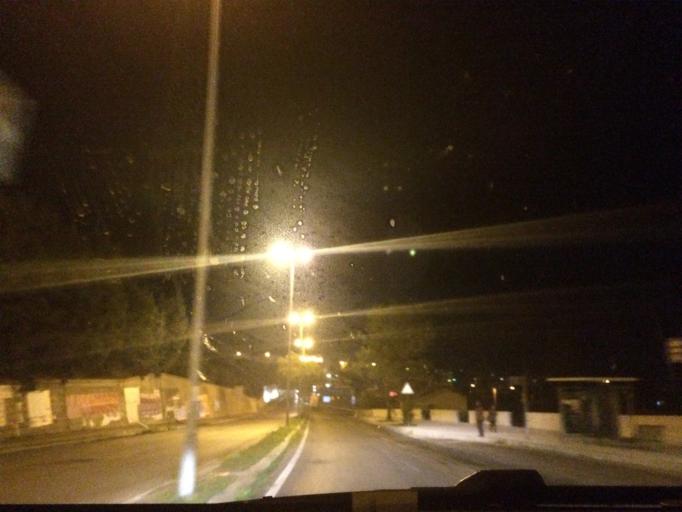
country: IT
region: Basilicate
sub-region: Provincia di Matera
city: Matera
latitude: 40.6562
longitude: 16.6119
